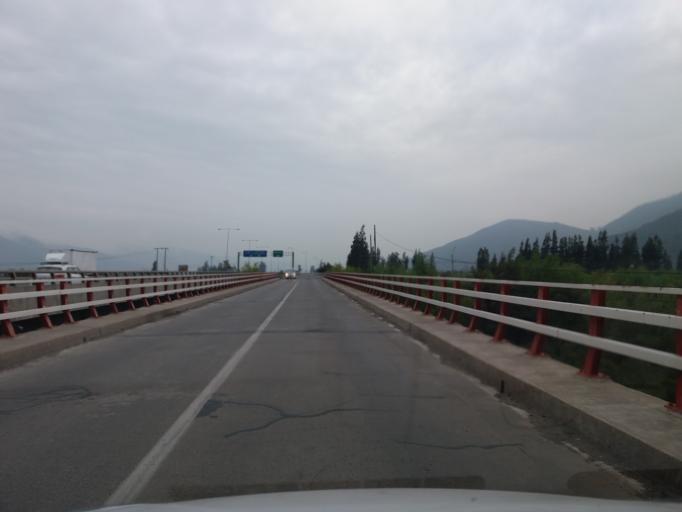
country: CL
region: Valparaiso
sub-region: Provincia de Quillota
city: Hacienda La Calera
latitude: -32.8441
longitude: -71.1054
